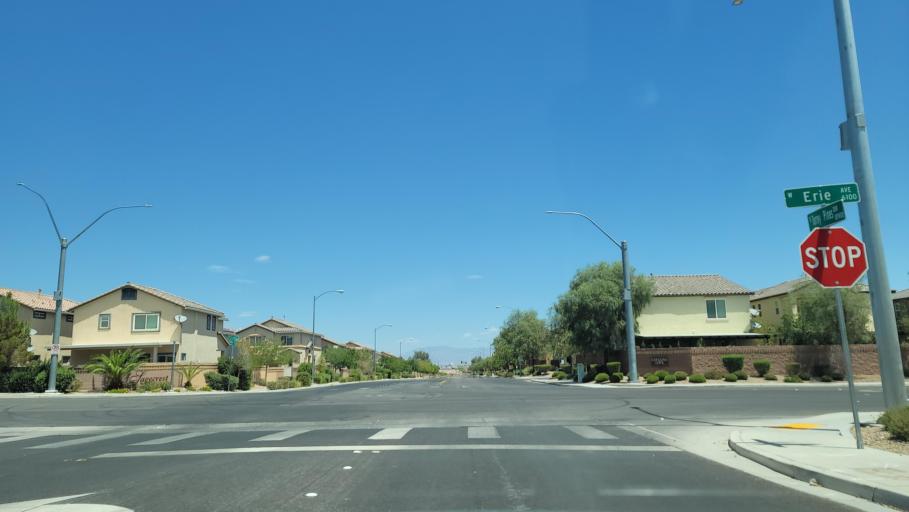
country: US
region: Nevada
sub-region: Clark County
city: Enterprise
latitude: 35.9911
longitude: -115.2345
